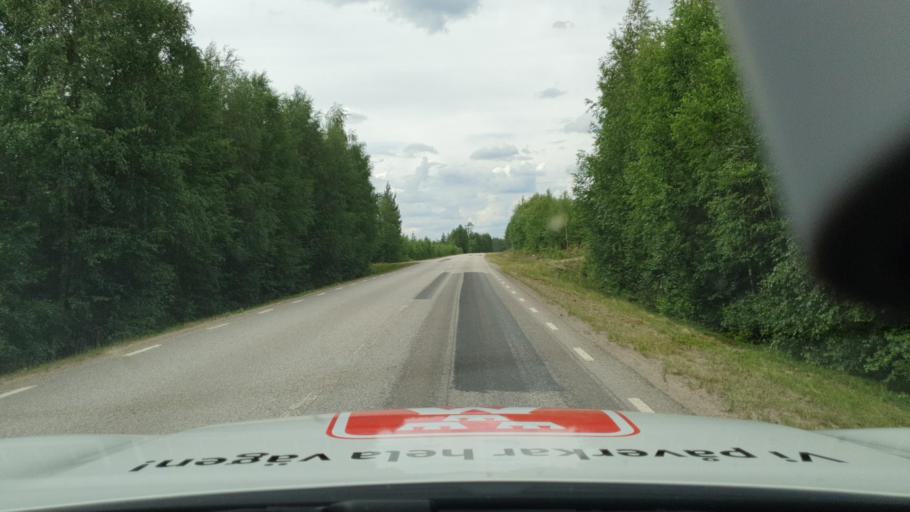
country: NO
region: Hedmark
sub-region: Trysil
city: Innbygda
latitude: 60.9364
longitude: 12.4831
